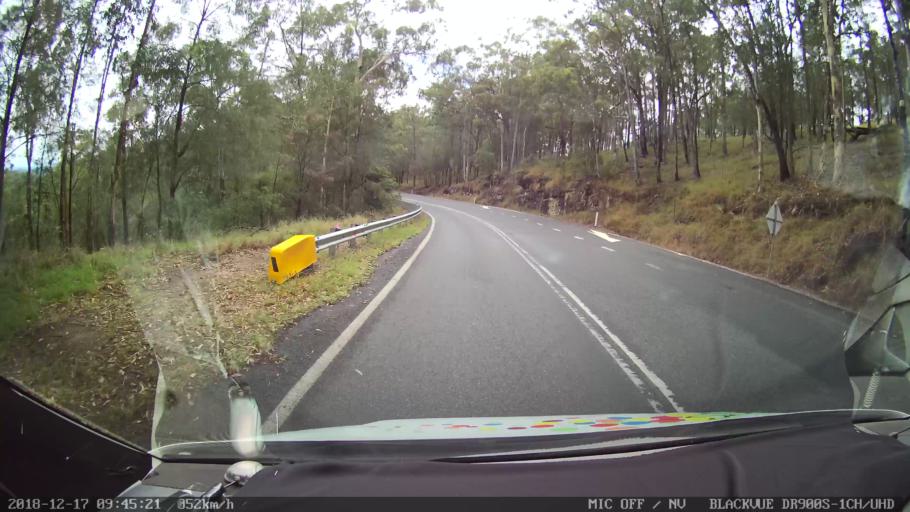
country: AU
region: New South Wales
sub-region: Tenterfield Municipality
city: Carrolls Creek
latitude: -28.9260
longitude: 152.3290
